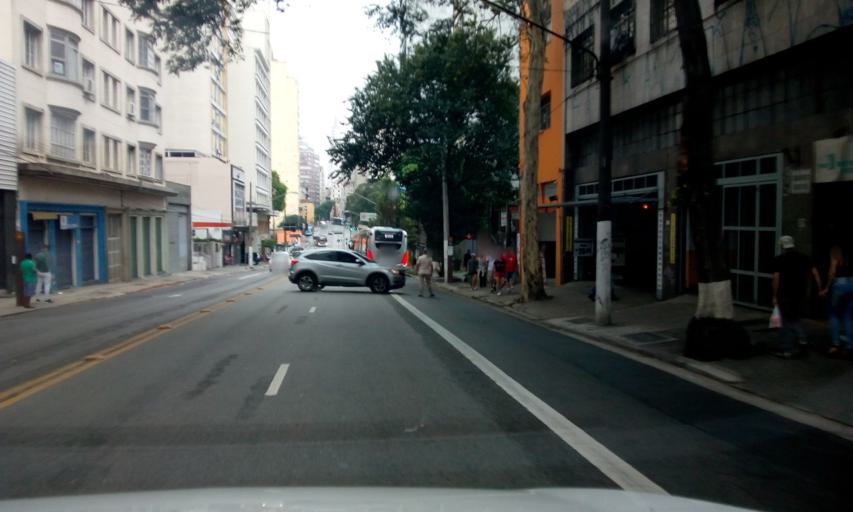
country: BR
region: Sao Paulo
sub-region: Sao Paulo
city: Sao Paulo
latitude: -23.5539
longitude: -46.6385
